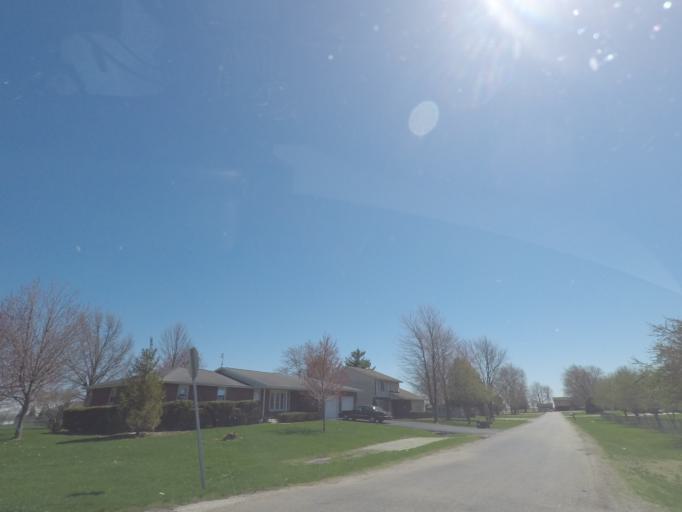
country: US
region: Illinois
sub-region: Macon County
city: Warrensburg
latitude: 39.9684
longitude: -89.1568
